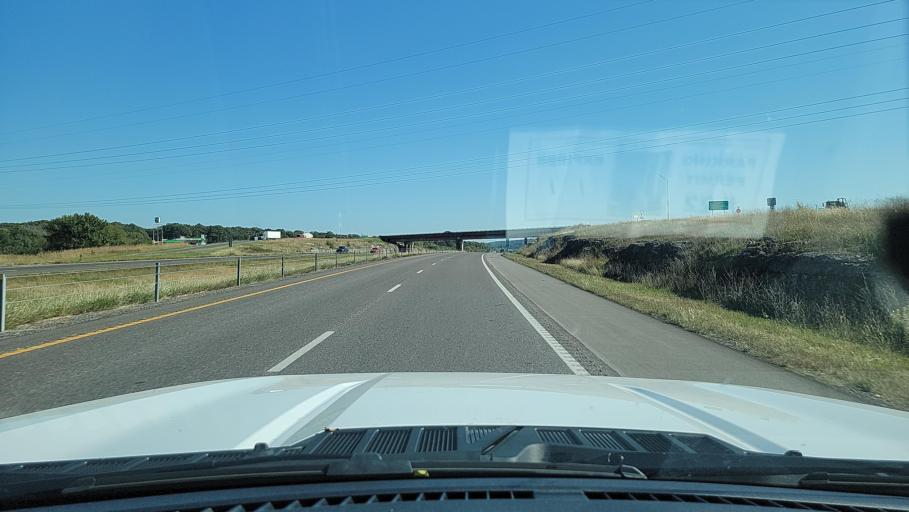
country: US
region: Missouri
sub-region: Sainte Genevieve County
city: Sainte Genevieve
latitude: 37.9379
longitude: -90.1250
